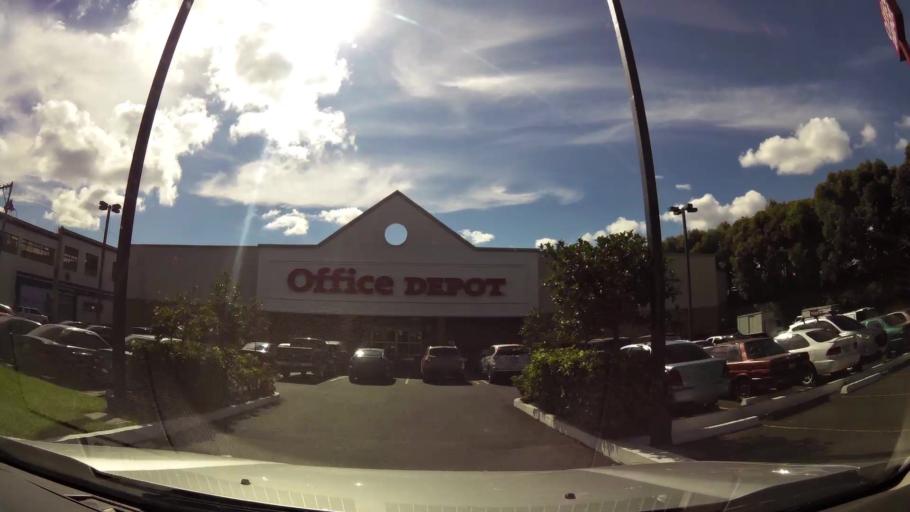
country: GT
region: Guatemala
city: Mixco
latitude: 14.6225
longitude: -90.5592
